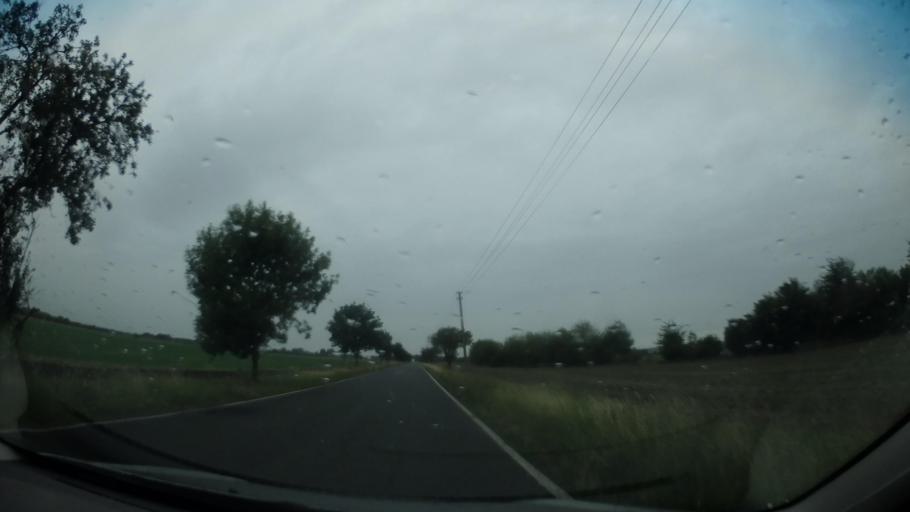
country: CZ
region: Central Bohemia
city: Loucen
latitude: 50.2364
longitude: 14.9846
